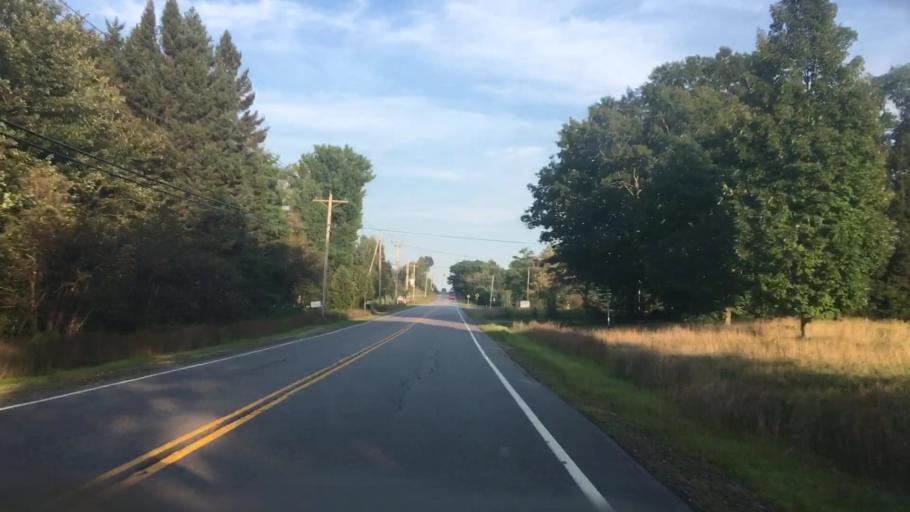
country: US
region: New Hampshire
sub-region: Belknap County
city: Gilmanton
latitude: 43.4251
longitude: -71.3337
